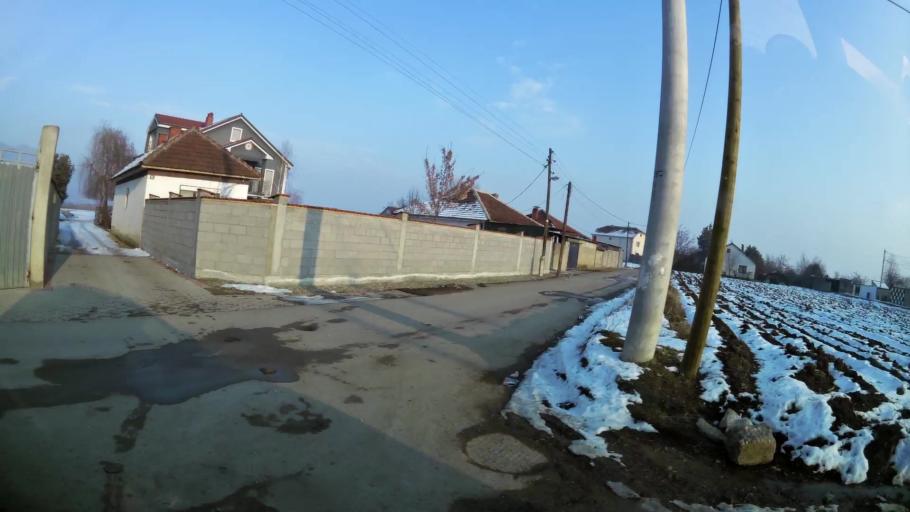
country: MK
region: Aracinovo
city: Arachinovo
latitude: 42.0114
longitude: 21.5299
